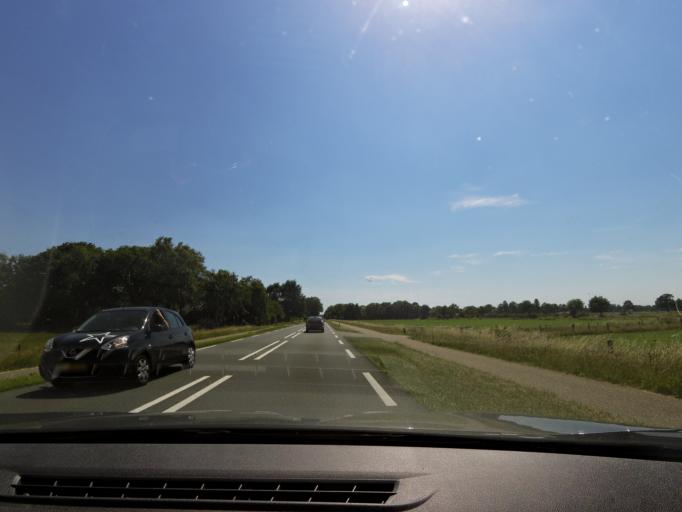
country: NL
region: Gelderland
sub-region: Berkelland
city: Eibergen
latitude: 52.0774
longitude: 6.6364
